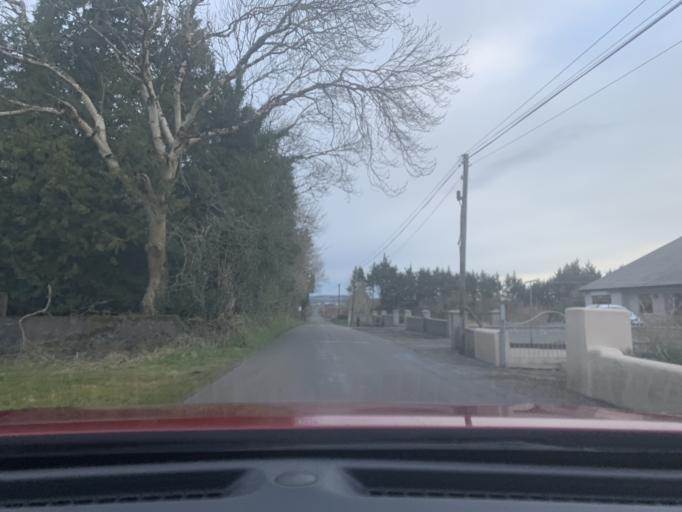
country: IE
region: Connaught
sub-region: Roscommon
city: Ballaghaderreen
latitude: 53.8807
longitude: -8.5642
